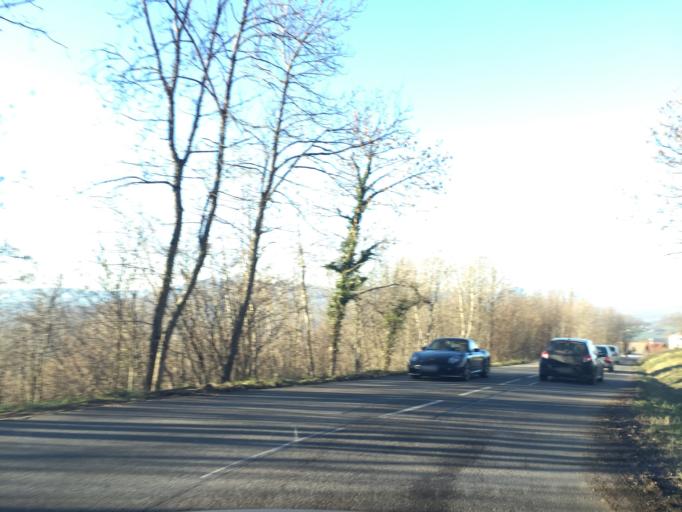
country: FR
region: Rhone-Alpes
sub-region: Departement de la Savoie
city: Mouxy
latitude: 45.6975
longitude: 5.9662
